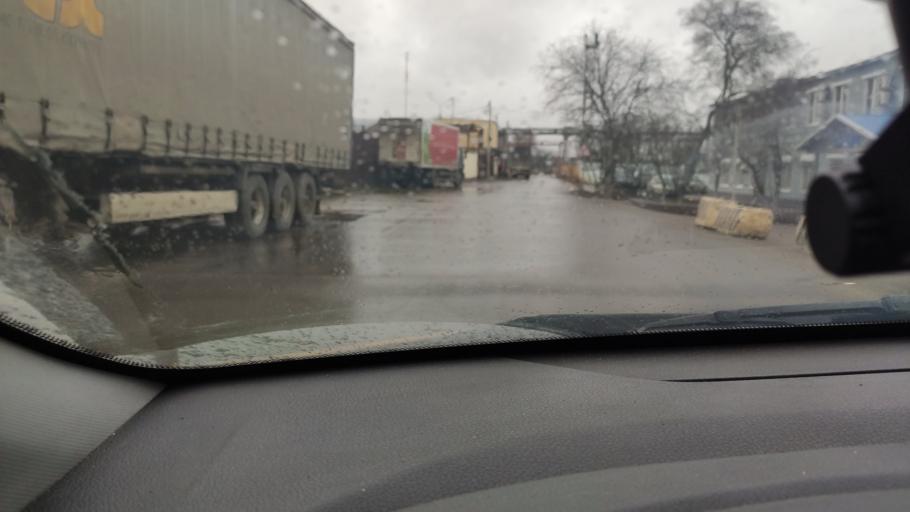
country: RU
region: Moskovskaya
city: Selyatino
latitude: 55.5132
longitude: 36.9660
